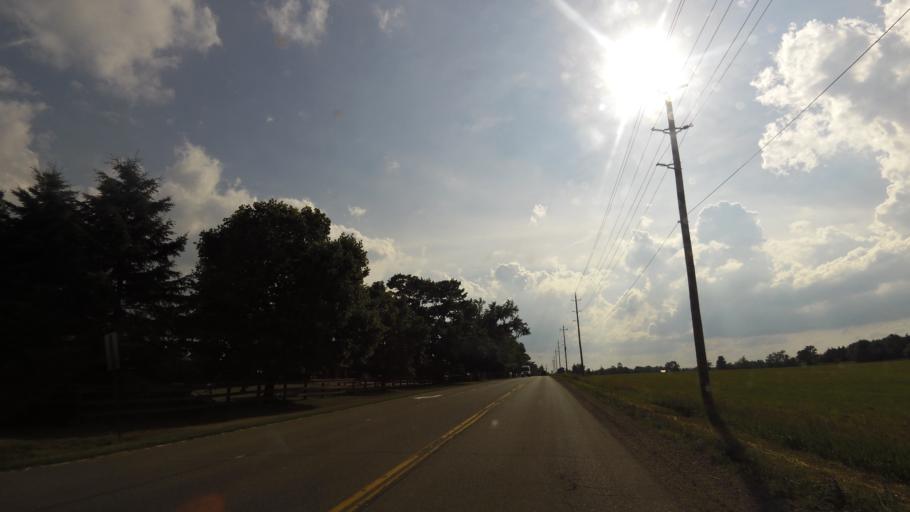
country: CA
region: Ontario
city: Orangeville
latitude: 43.9521
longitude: -80.0739
